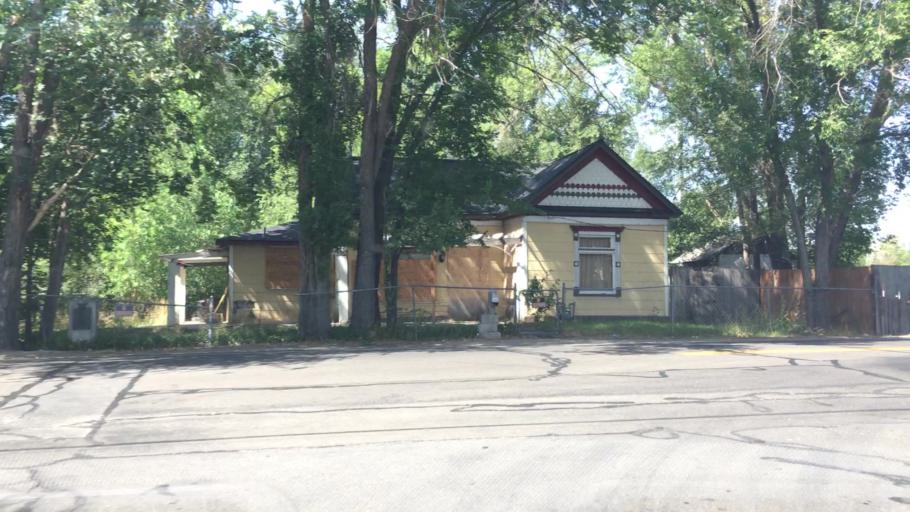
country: US
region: Utah
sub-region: Salt Lake County
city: Millcreek
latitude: 40.6790
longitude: -111.8842
